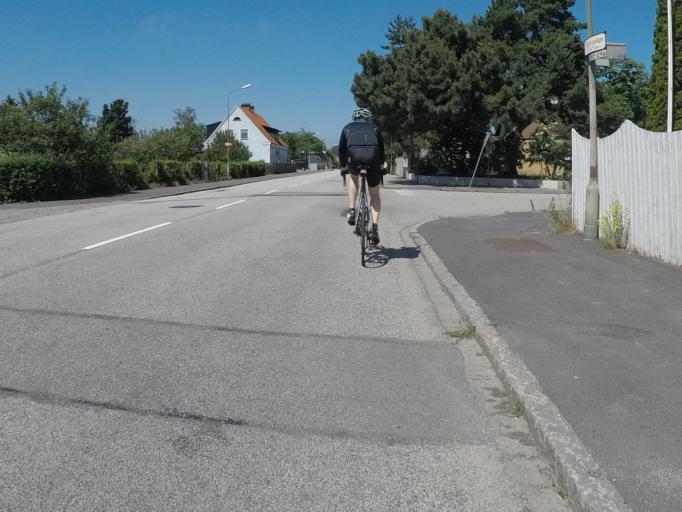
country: SE
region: Skane
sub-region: Burlovs Kommun
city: Arloev
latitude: 55.5905
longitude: 13.0796
